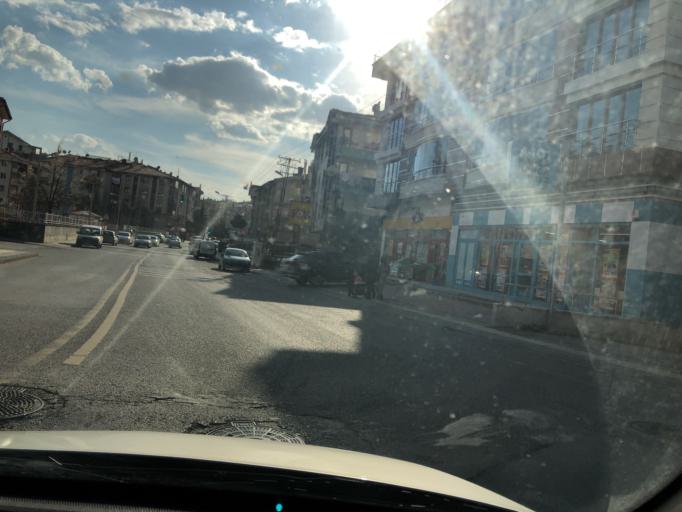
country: TR
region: Ankara
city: Ankara
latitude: 39.9834
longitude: 32.8411
